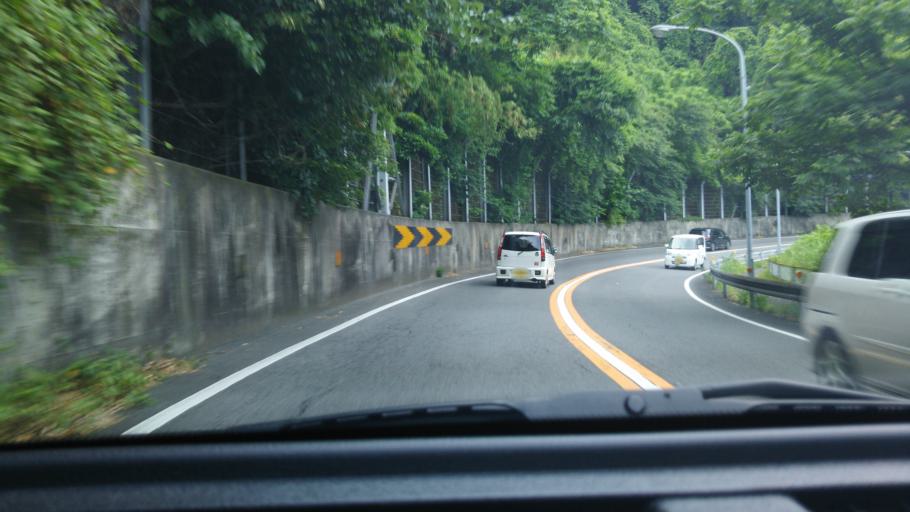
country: JP
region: Shizuoka
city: Ito
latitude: 34.8715
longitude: 139.0958
